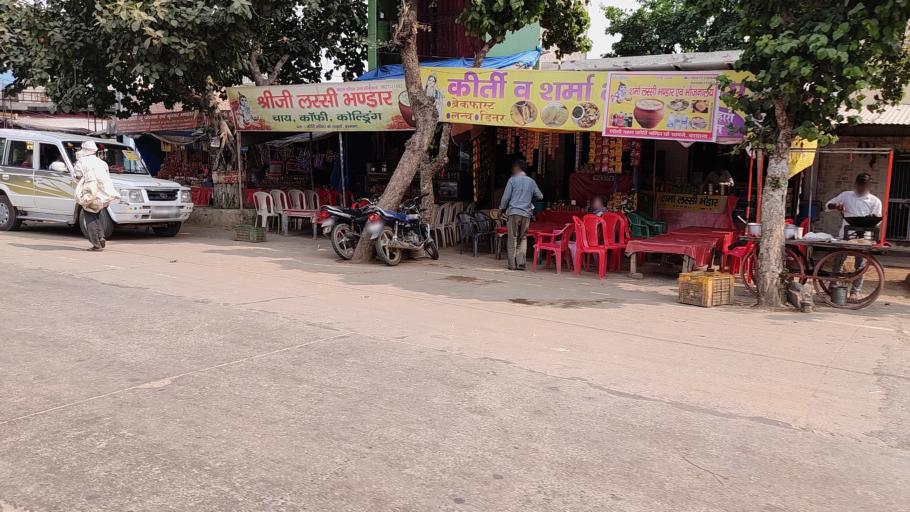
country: IN
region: Uttar Pradesh
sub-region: Mathura
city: Barsana
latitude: 27.6541
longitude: 77.3810
